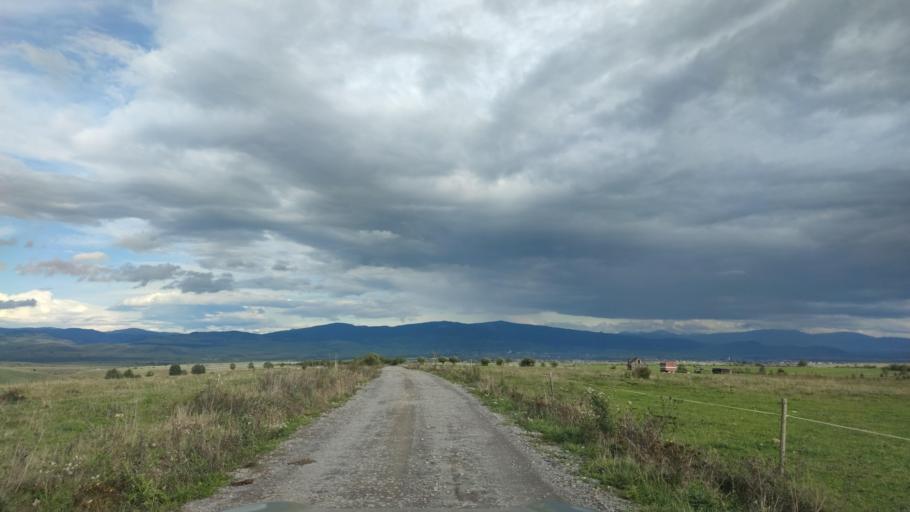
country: RO
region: Harghita
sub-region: Comuna Remetea
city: Remetea
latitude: 46.8156
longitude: 25.3792
